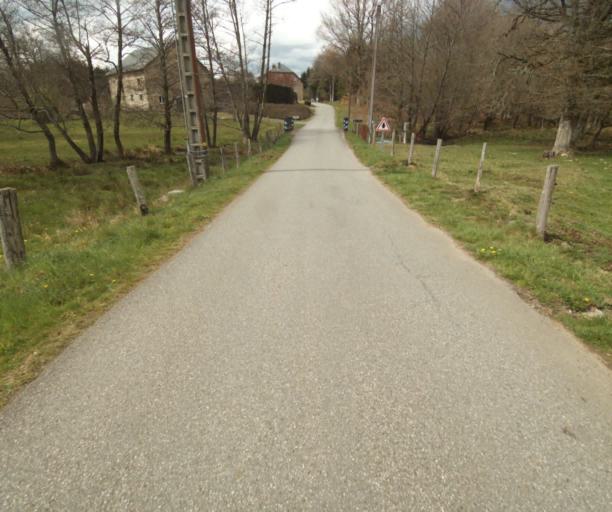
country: FR
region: Limousin
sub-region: Departement de la Correze
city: Correze
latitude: 45.3339
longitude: 1.9229
